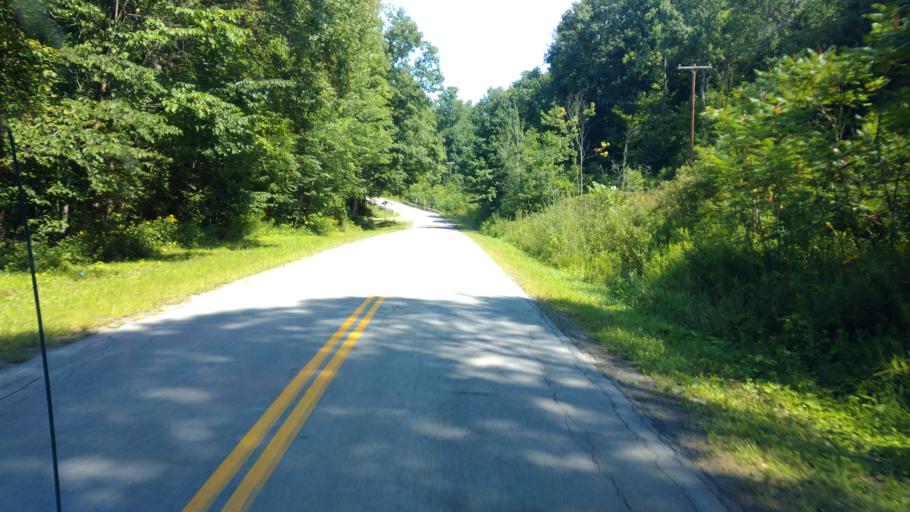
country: US
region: New York
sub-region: Allegany County
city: Belmont
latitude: 42.2871
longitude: -78.0534
